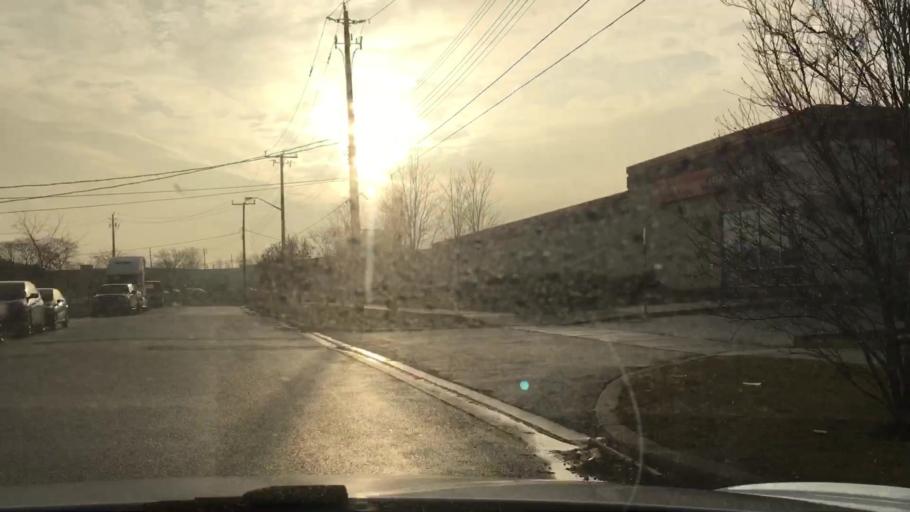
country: CA
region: Ontario
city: Scarborough
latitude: 43.7831
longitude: -79.2375
